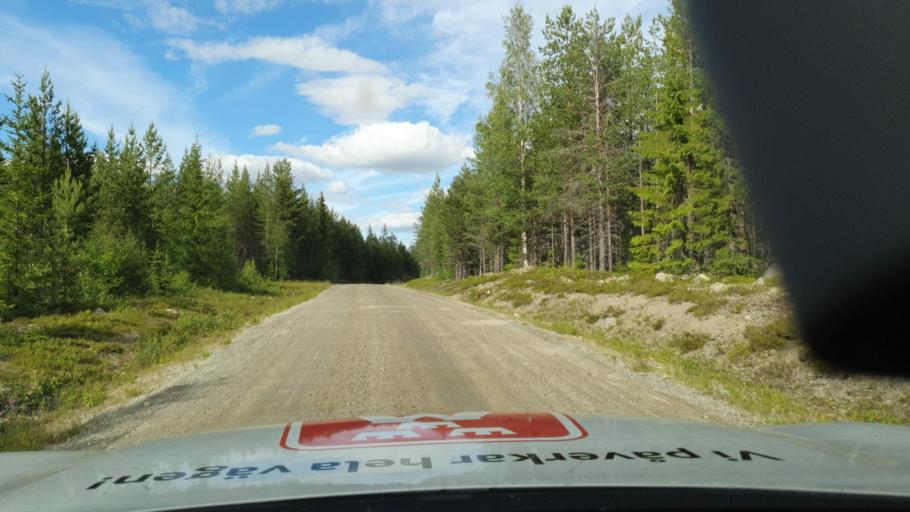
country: SE
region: Vaesterbotten
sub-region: Lycksele Kommun
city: Soderfors
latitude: 64.2605
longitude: 18.0838
